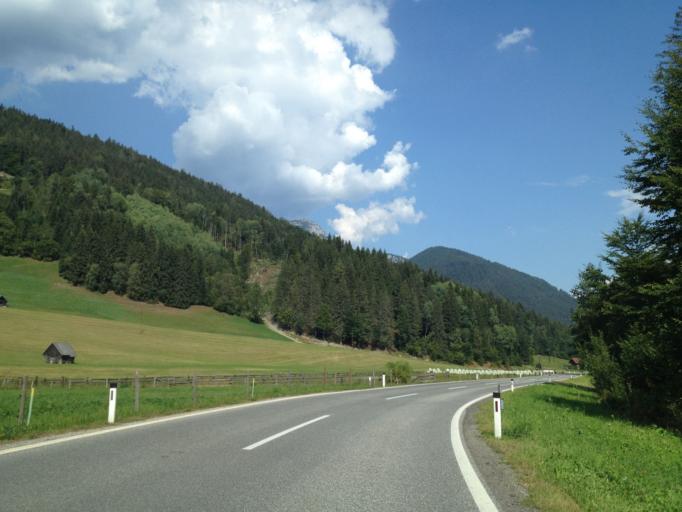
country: AT
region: Styria
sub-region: Politischer Bezirk Liezen
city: Haus im Ennstal
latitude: 47.4247
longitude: 13.7647
